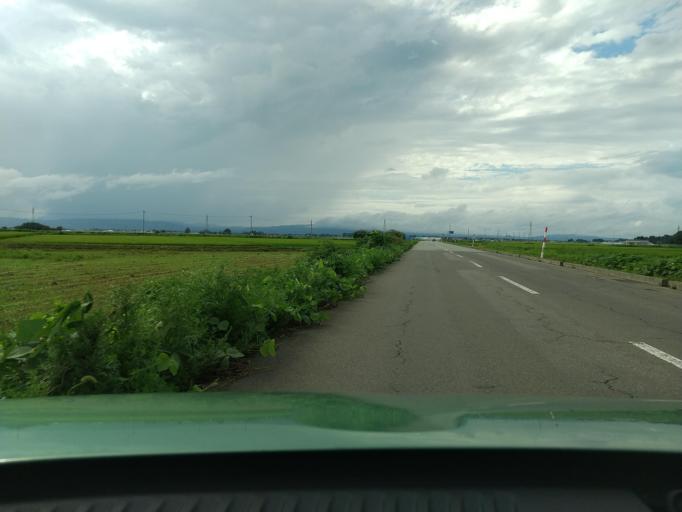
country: JP
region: Akita
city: Yuzawa
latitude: 39.2357
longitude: 140.5085
